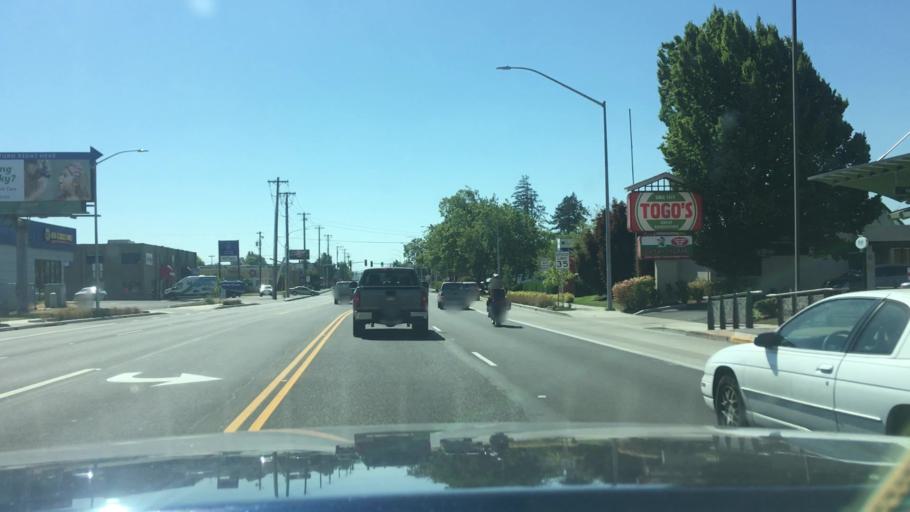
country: US
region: Oregon
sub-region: Lane County
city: Eugene
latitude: 44.0475
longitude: -123.1412
